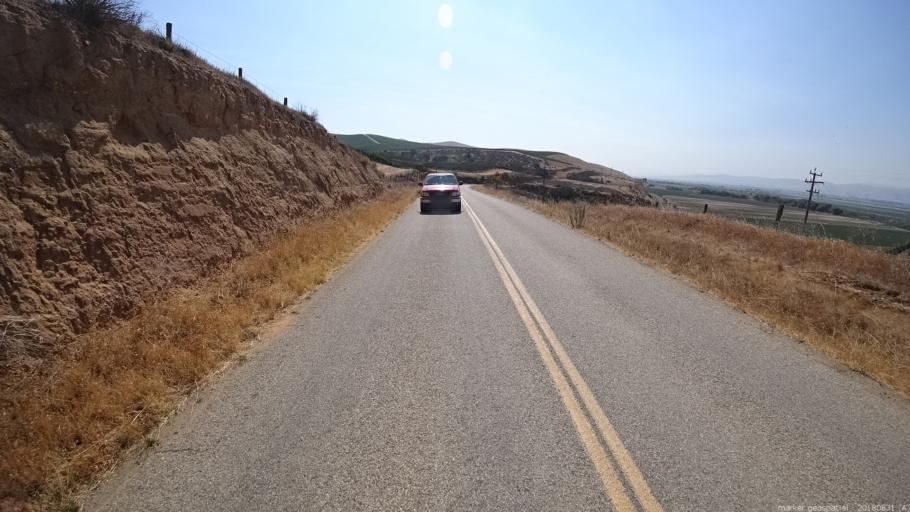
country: US
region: California
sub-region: Monterey County
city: Soledad
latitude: 36.4005
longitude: -121.2537
